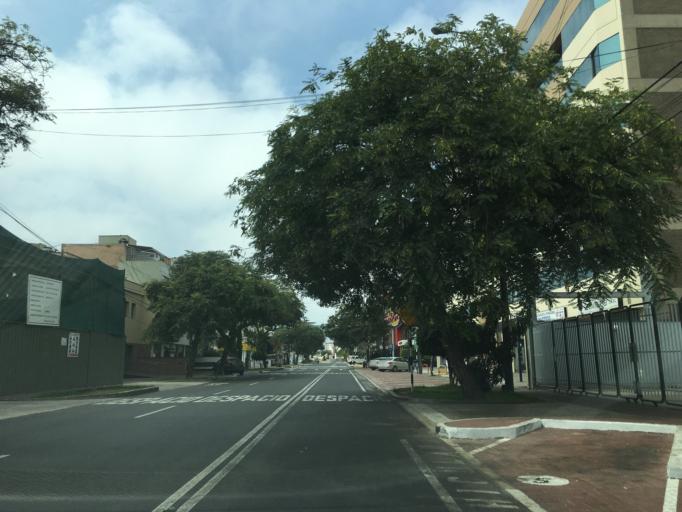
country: PE
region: Lima
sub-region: Lima
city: San Isidro
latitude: -12.1084
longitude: -77.0388
